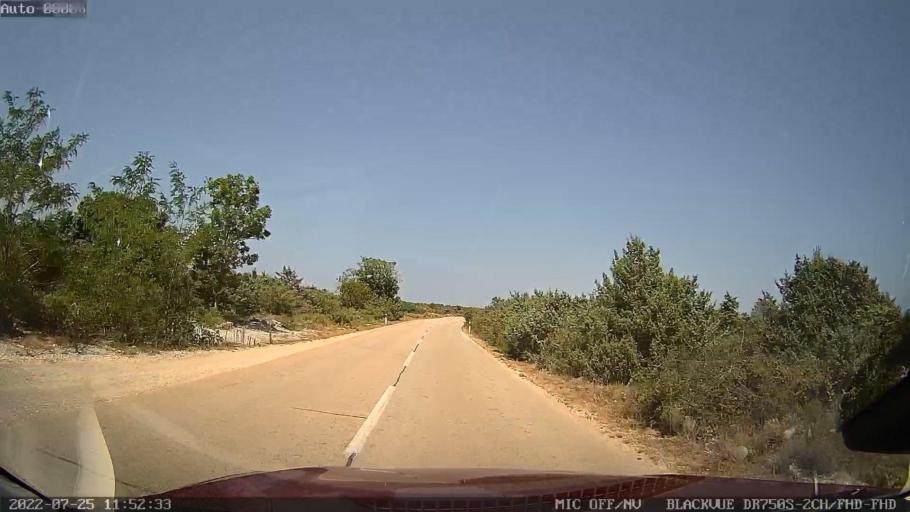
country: HR
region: Zadarska
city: Vrsi
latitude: 44.2487
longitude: 15.2426
